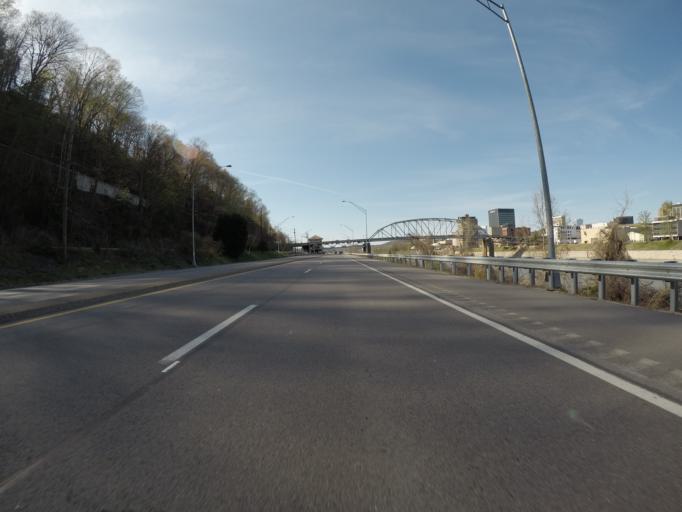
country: US
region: West Virginia
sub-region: Kanawha County
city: Charleston
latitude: 38.3443
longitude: -81.6357
